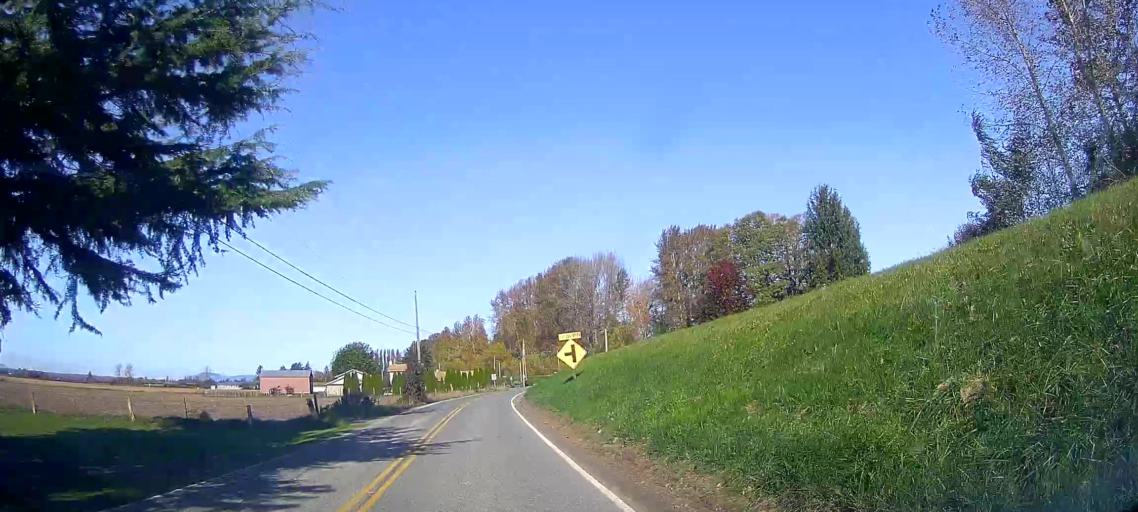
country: US
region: Washington
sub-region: Skagit County
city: Mount Vernon
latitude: 48.4049
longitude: -122.3682
